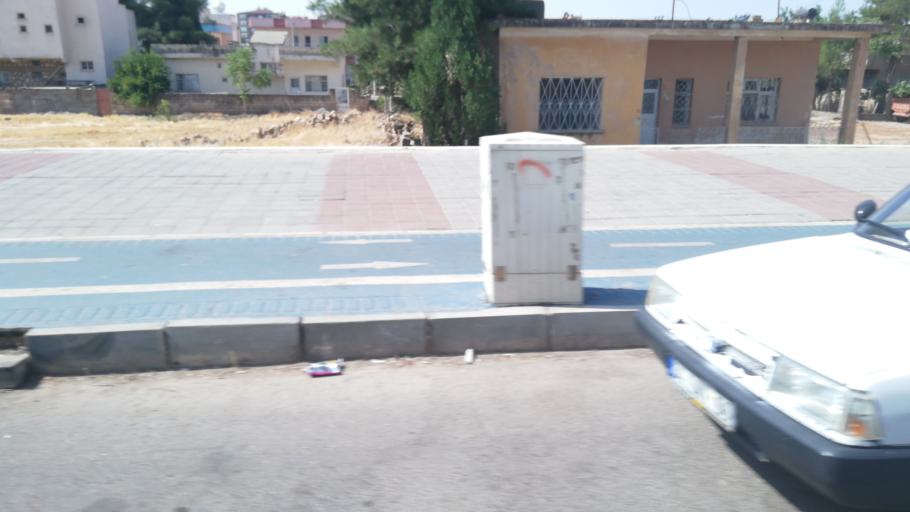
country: TR
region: Mardin
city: Midyat
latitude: 37.4211
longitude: 41.3495
